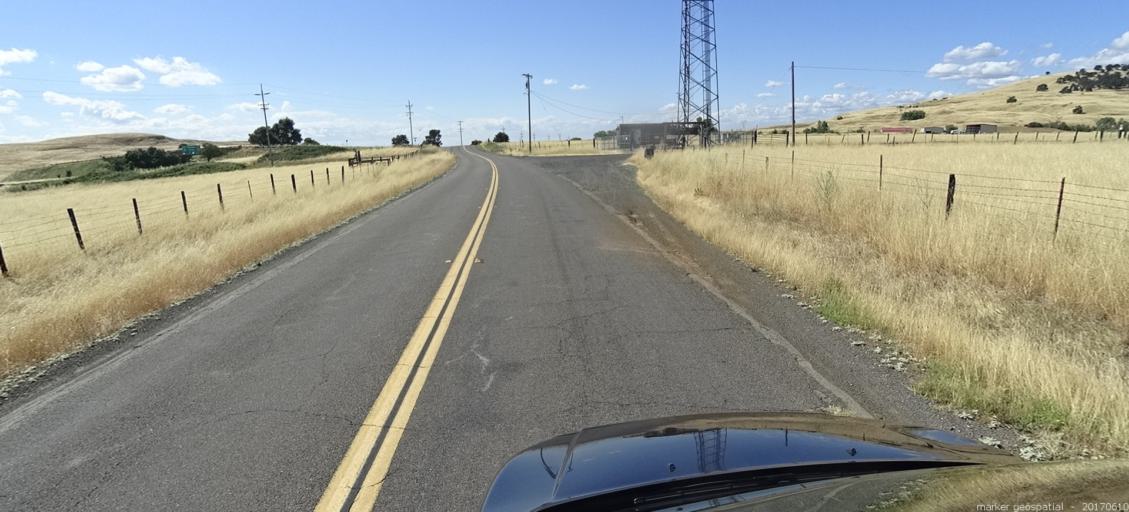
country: US
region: California
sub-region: Butte County
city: Thermalito
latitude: 39.5664
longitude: -121.6073
